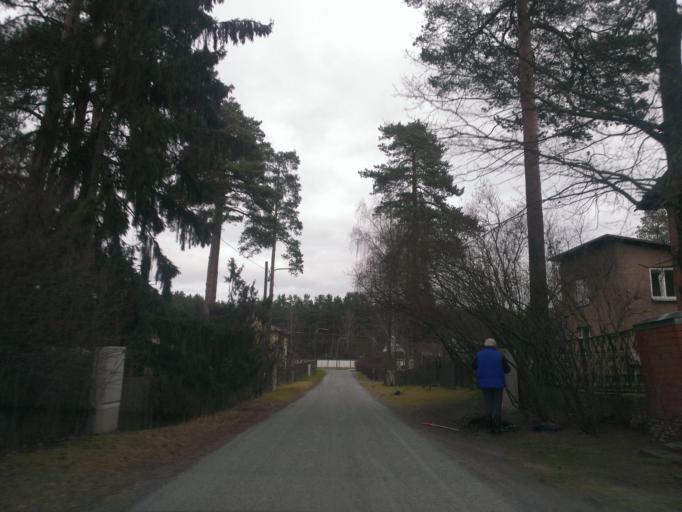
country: LV
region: Riga
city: Bergi
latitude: 56.9904
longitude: 24.3025
